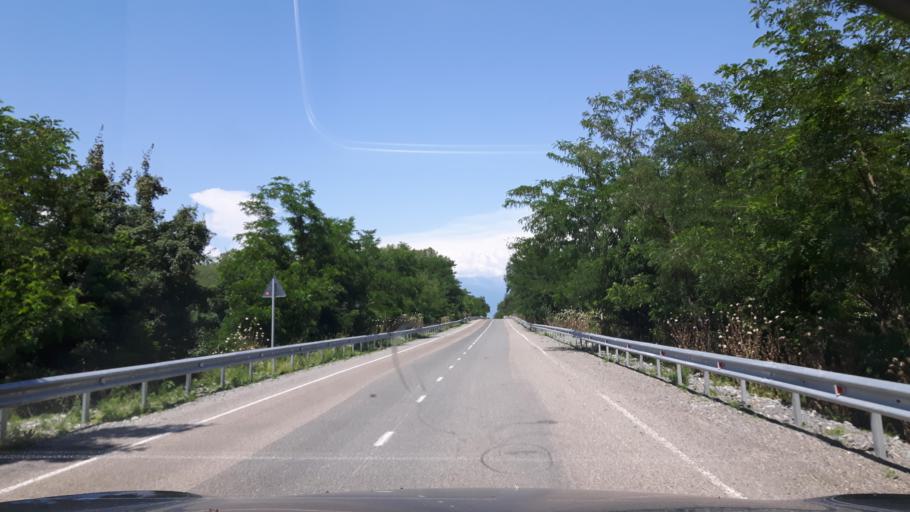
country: GE
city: Tsnori
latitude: 41.6734
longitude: 46.0811
